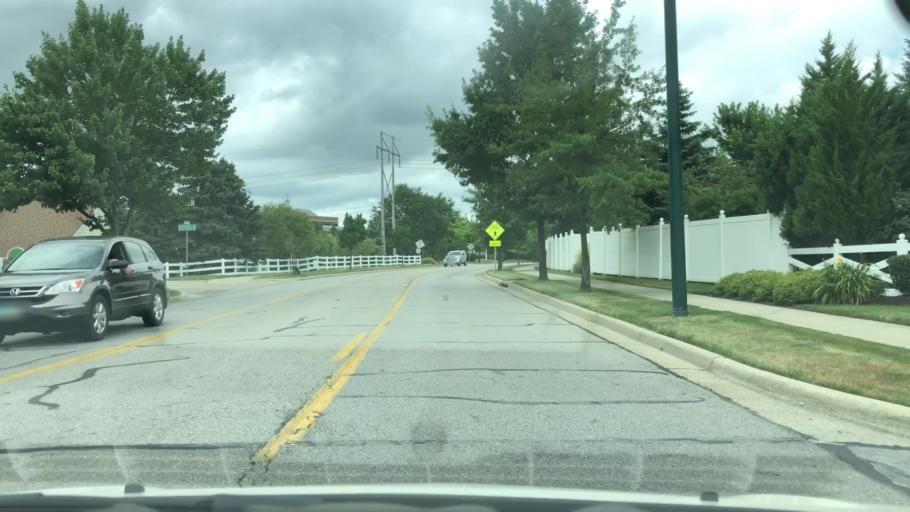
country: US
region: Ohio
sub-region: Franklin County
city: Westerville
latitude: 40.1371
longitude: -82.9212
